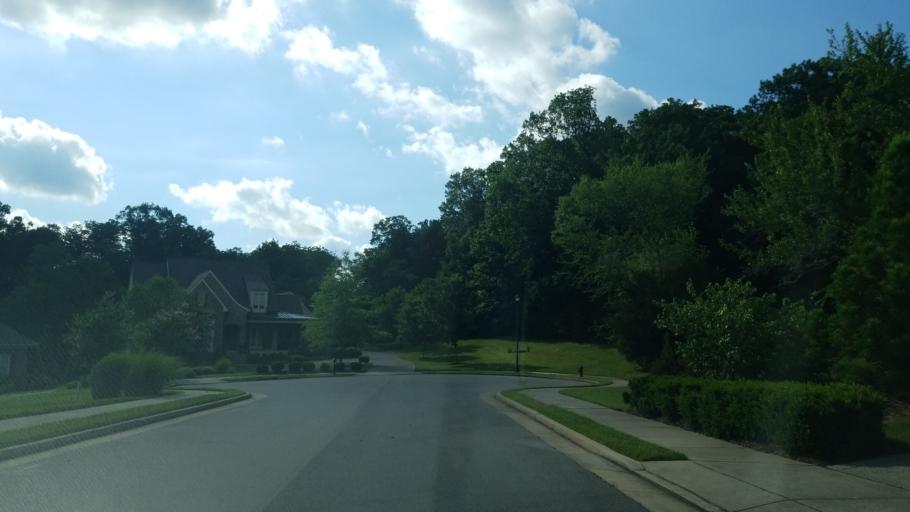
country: US
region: Tennessee
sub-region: Davidson County
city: Forest Hills
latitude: 36.0305
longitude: -86.8542
